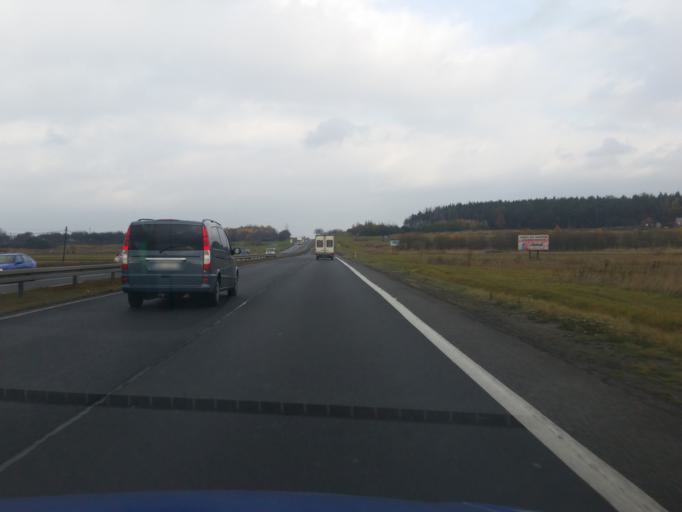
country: PL
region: Silesian Voivodeship
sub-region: Powiat myszkowski
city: Kozieglowy
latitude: 50.5563
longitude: 19.1772
